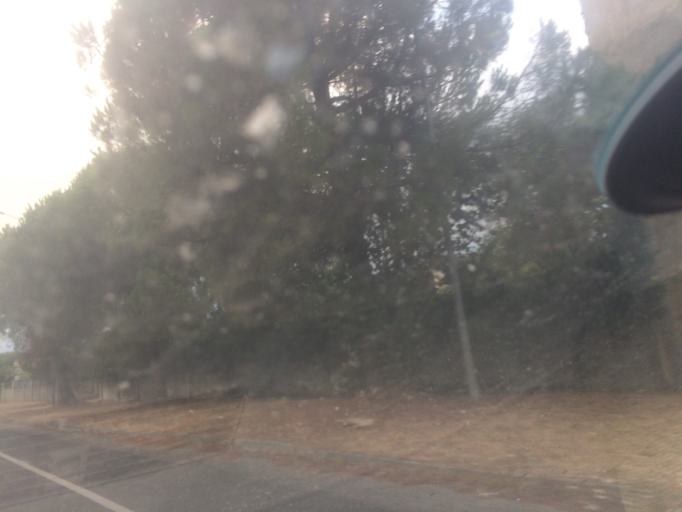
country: IT
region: Tuscany
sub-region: Provincia di Massa-Carrara
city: Massa
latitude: 44.0288
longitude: 10.1041
